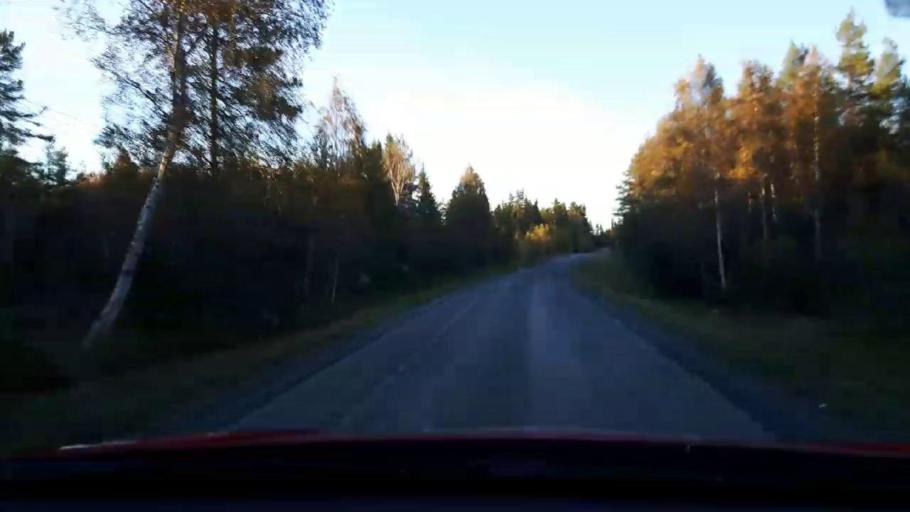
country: SE
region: Jaemtland
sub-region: Krokoms Kommun
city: Krokom
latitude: 63.4401
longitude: 14.4214
